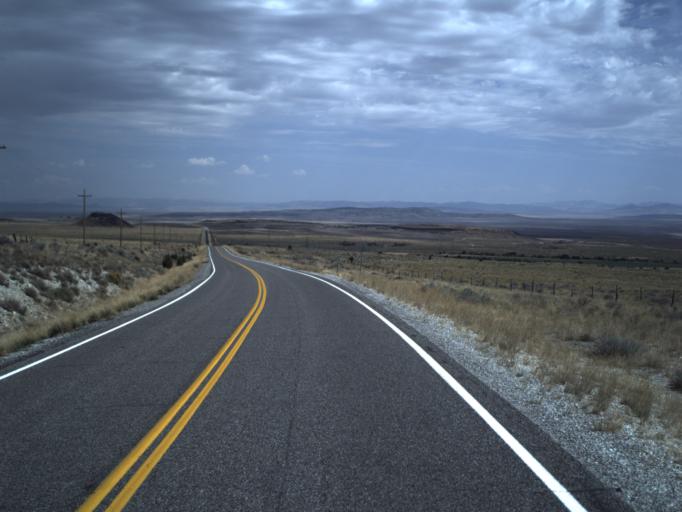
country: US
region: Idaho
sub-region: Cassia County
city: Burley
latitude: 41.8150
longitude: -113.2133
